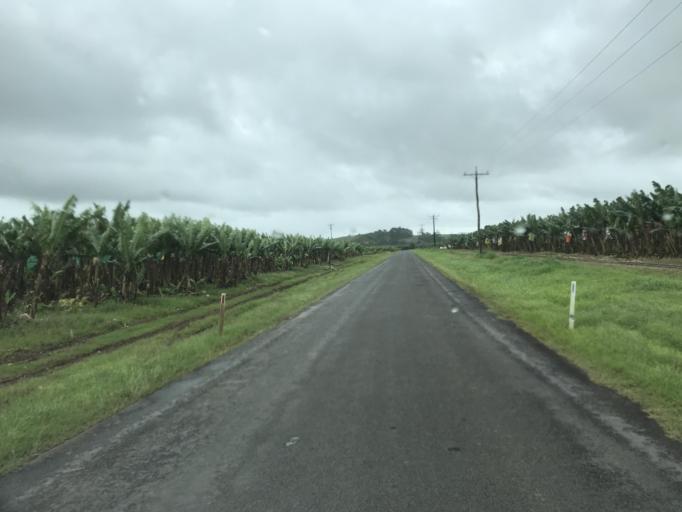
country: AU
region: Queensland
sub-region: Cassowary Coast
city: Innisfail
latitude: -17.5099
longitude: 145.9788
